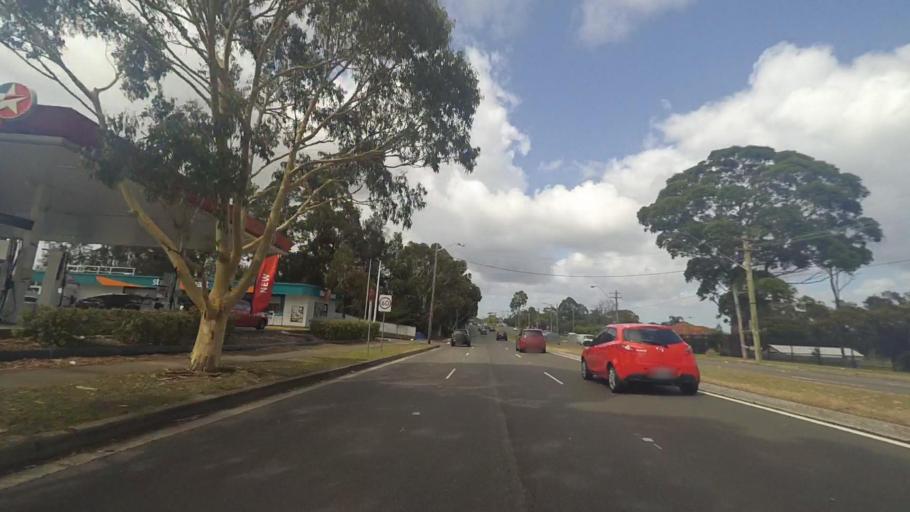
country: AU
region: New South Wales
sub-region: Sutherland Shire
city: Heathcote
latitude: -34.0884
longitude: 151.0068
